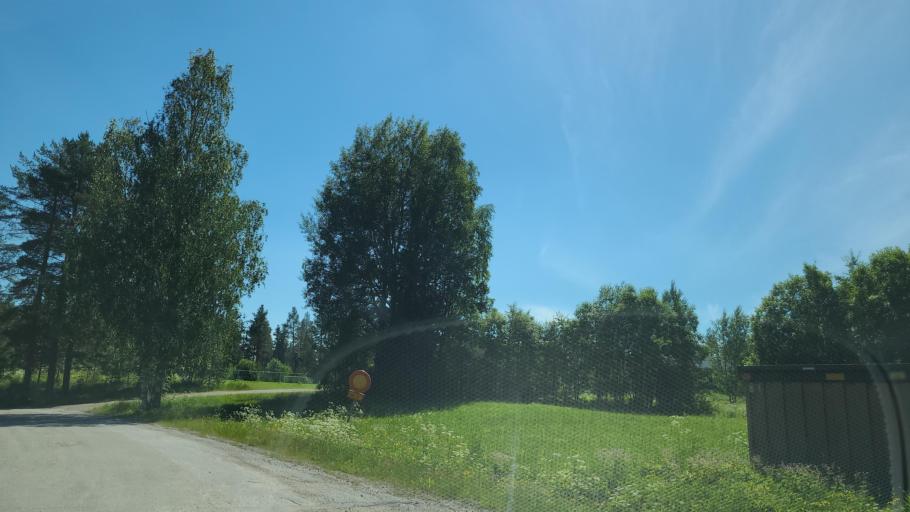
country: SE
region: Vaesterbotten
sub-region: Bjurholms Kommun
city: Bjurholm
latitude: 63.6903
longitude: 18.8642
